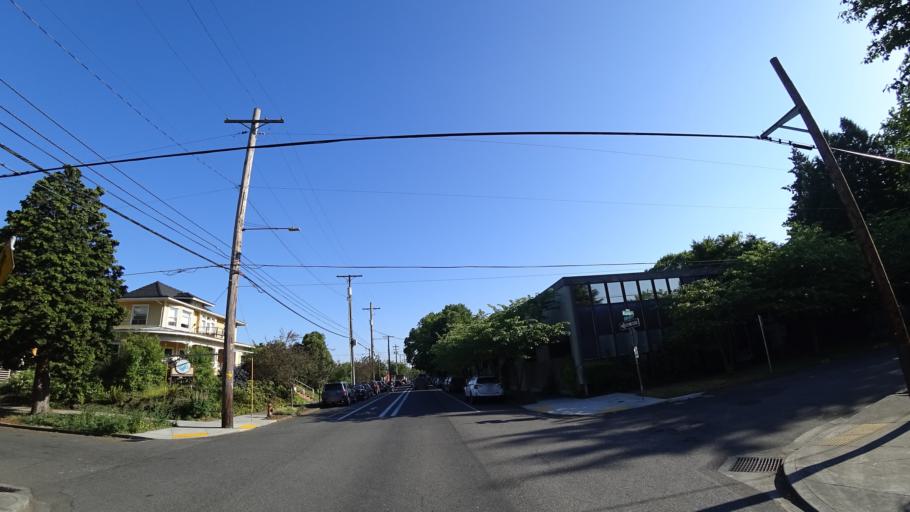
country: US
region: Oregon
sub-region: Multnomah County
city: Portland
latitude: 45.5604
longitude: -122.6669
